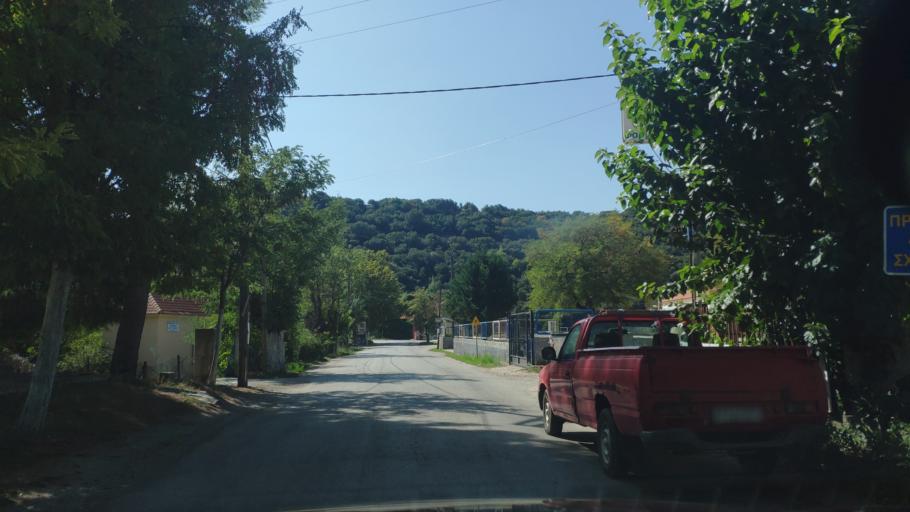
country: GR
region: Peloponnese
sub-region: Nomos Korinthias
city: Nemea
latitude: 37.8889
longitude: 22.4975
